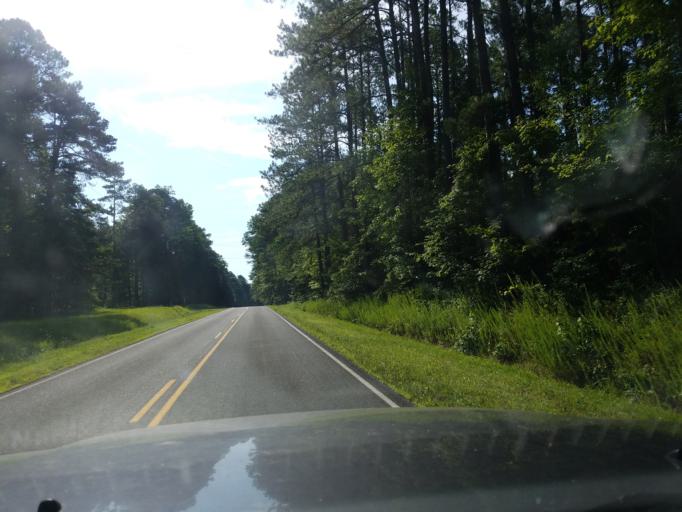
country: US
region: North Carolina
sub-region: Granville County
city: Butner
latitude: 36.1839
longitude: -78.8136
